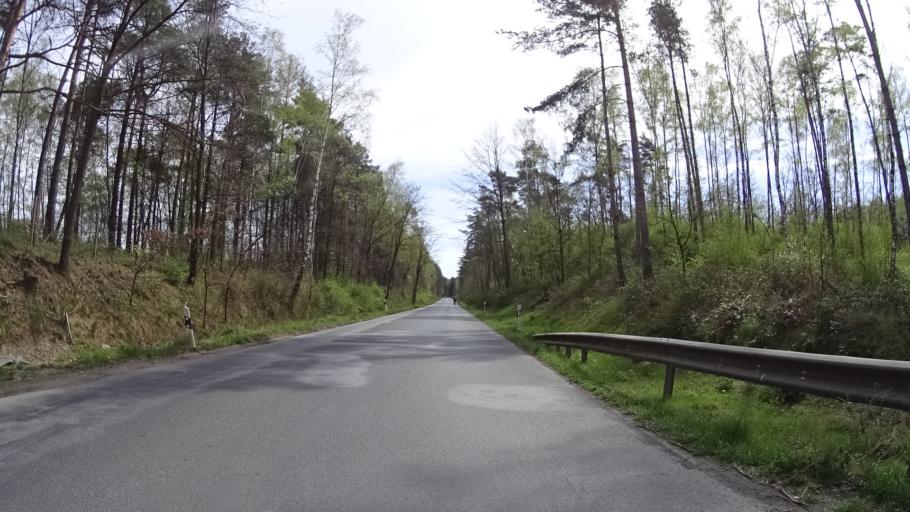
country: DE
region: Lower Saxony
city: Lingen
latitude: 52.4691
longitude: 7.3194
